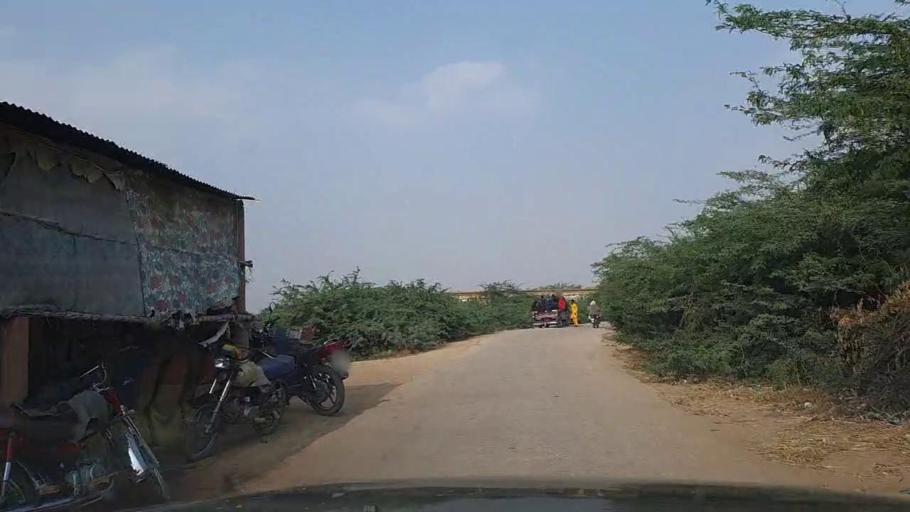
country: PK
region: Sindh
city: Thatta
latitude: 24.8558
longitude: 67.7759
